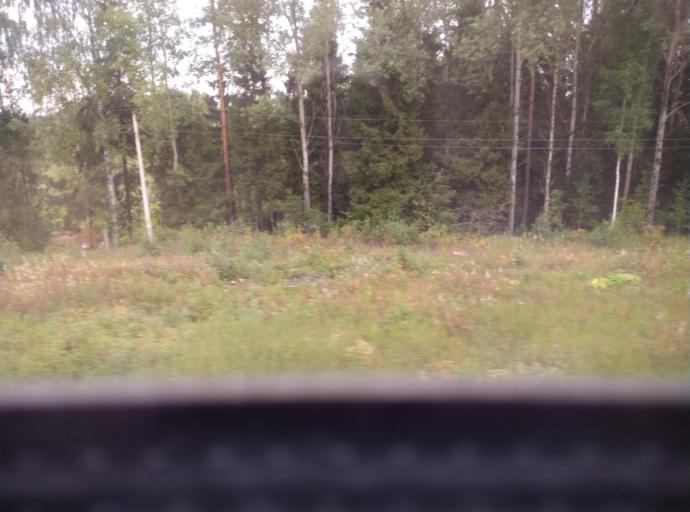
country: RU
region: Kostroma
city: Nerekhta
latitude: 57.4426
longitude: 40.4169
